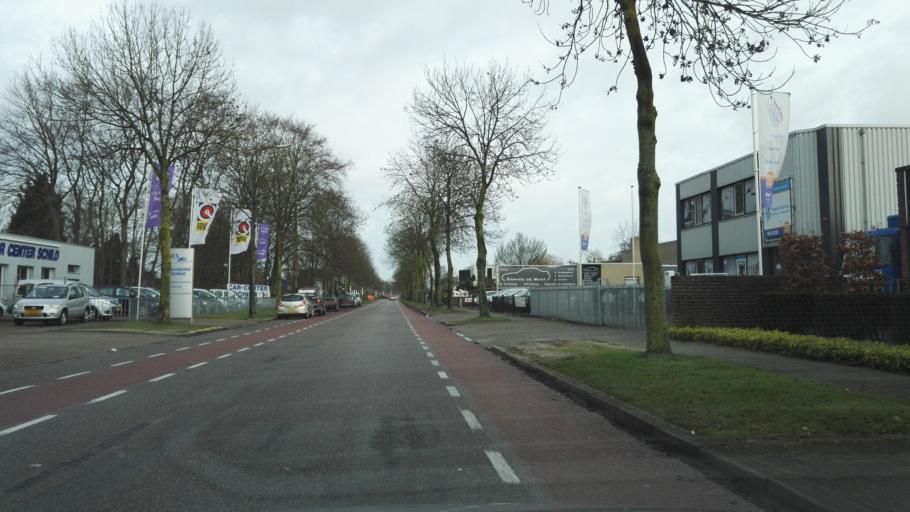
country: NL
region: Gelderland
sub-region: Gemeente Apeldoorn
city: Apeldoorn
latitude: 52.2237
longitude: 5.9754
